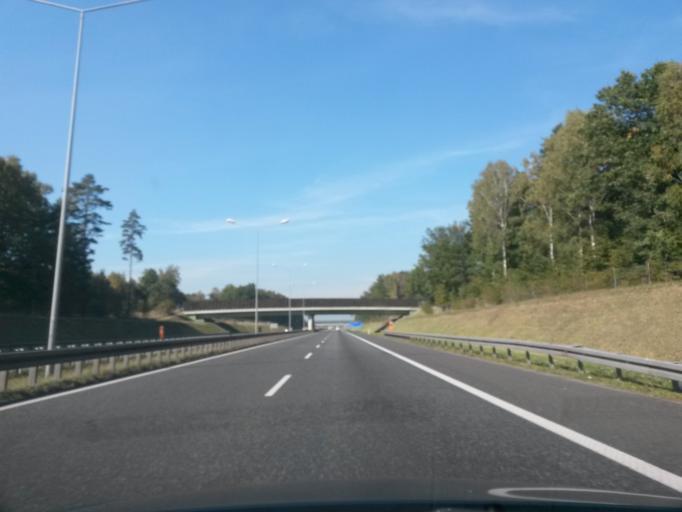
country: PL
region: Silesian Voivodeship
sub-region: Powiat gliwicki
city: Sosnicowice
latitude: 50.2853
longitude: 18.5673
